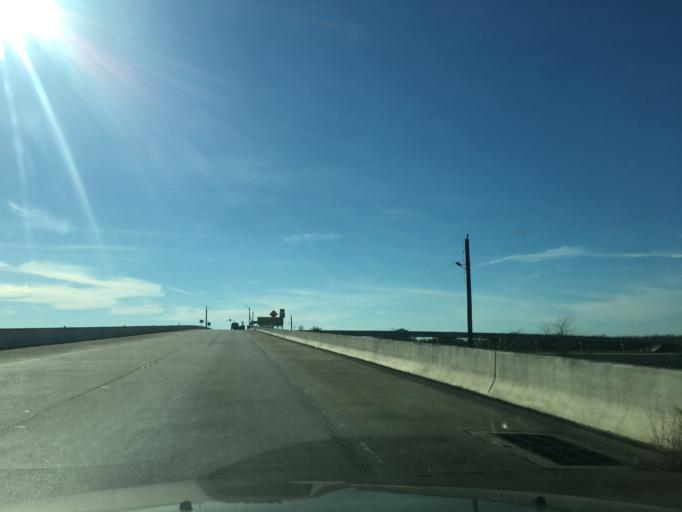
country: US
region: Texas
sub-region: Fort Bend County
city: Rosenberg
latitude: 29.5256
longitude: -95.8724
